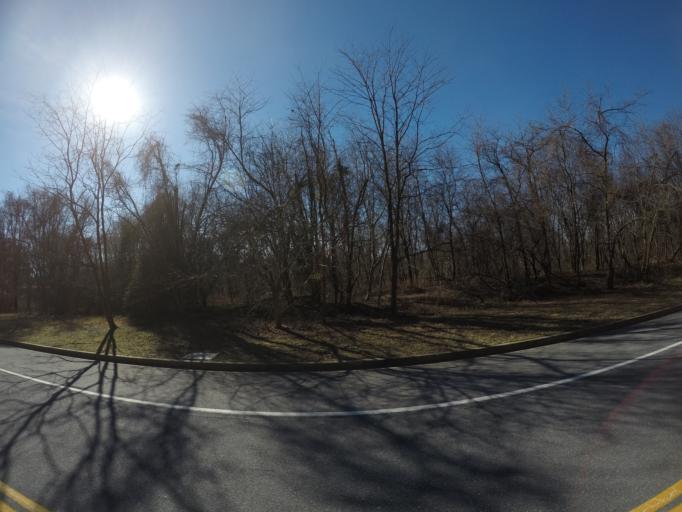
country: US
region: Maryland
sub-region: Howard County
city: Columbia
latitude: 39.2374
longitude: -76.8304
